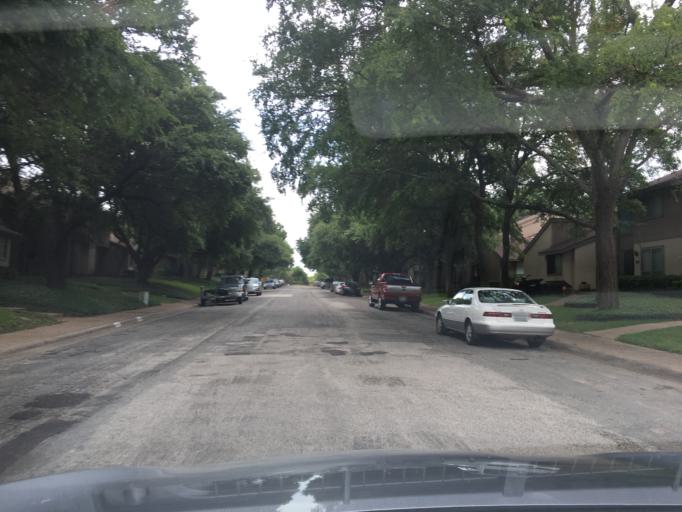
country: US
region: Texas
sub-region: Dallas County
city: Richardson
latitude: 32.9111
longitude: -96.7117
